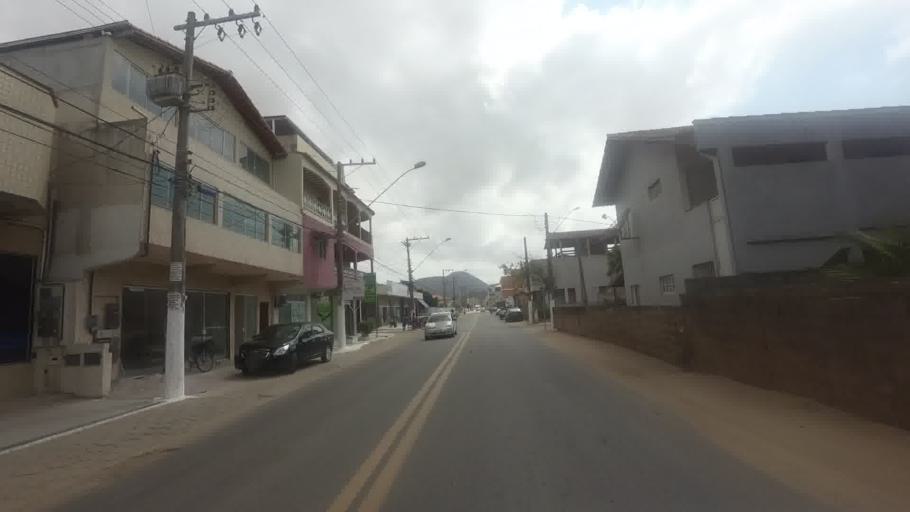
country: BR
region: Espirito Santo
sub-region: Piuma
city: Piuma
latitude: -20.8986
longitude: -40.7775
